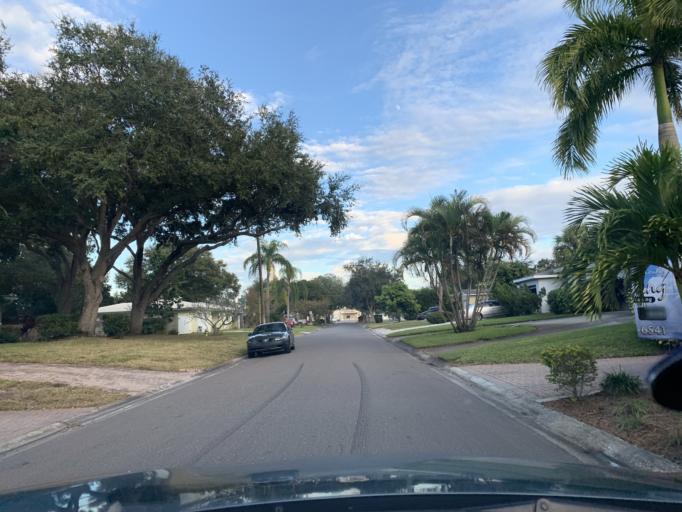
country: US
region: Florida
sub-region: Pinellas County
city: Bay Pines
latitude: 27.8078
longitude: -82.7561
